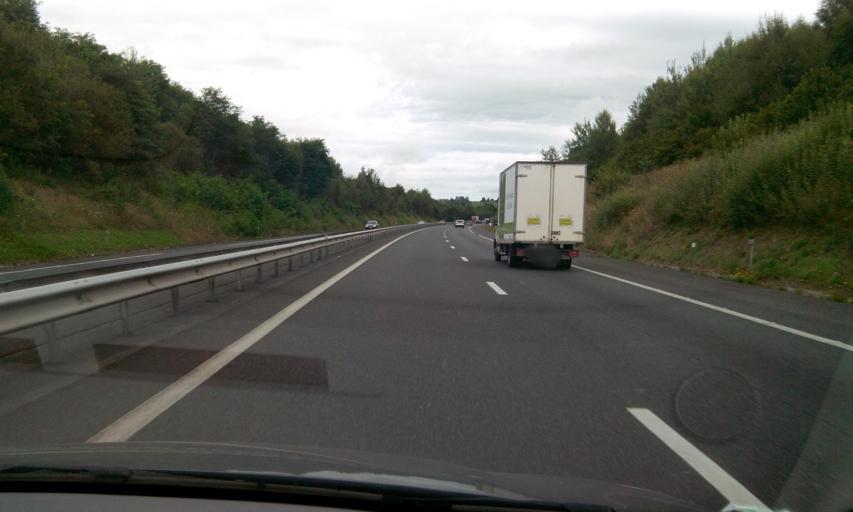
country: FR
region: Limousin
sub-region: Departement de la Correze
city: Vigeois
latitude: 45.4158
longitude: 1.5211
